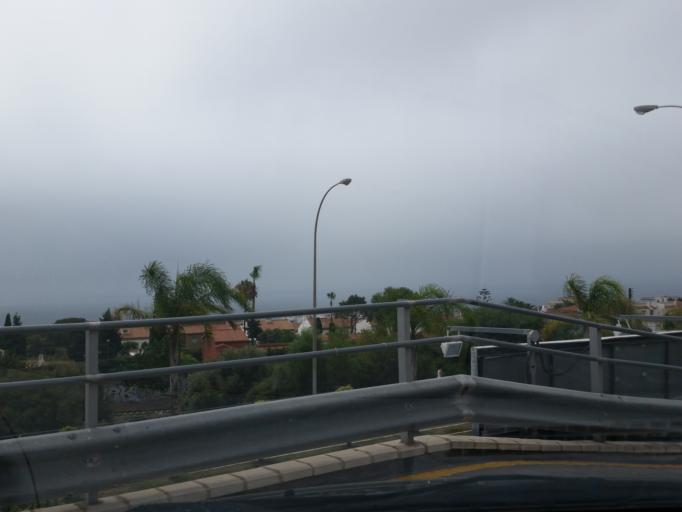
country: ES
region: Andalusia
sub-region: Provincia de Malaga
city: Torremolinos
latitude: 36.6130
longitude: -4.5117
